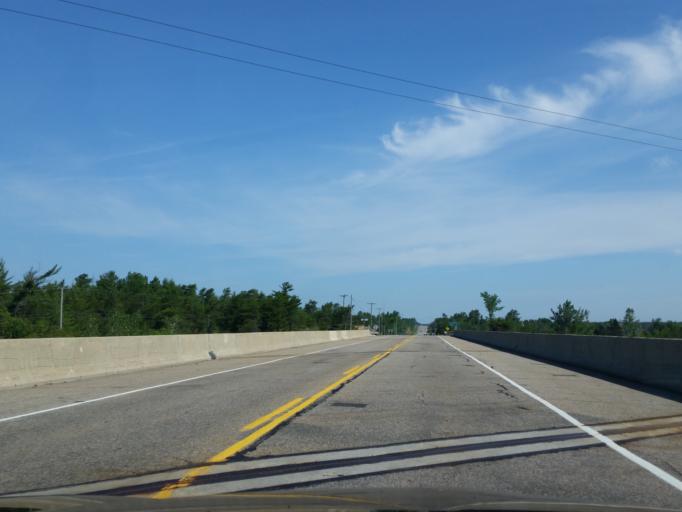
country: CA
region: Ontario
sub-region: Parry Sound District
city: Parry Sound
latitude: 45.8001
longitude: -80.5359
